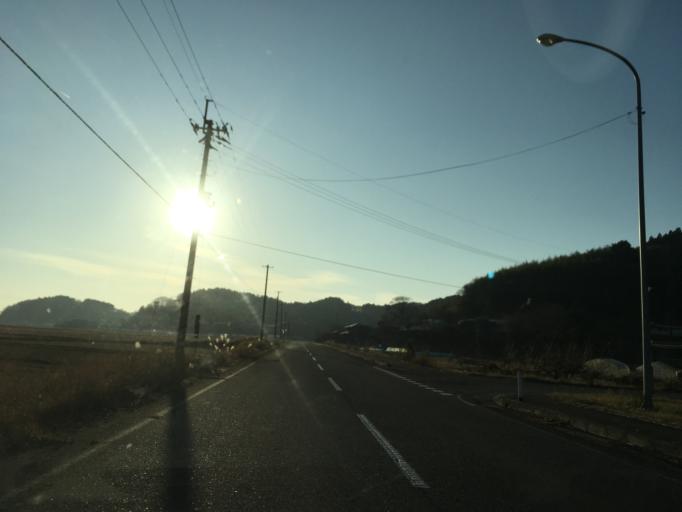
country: JP
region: Iwate
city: Ichinoseki
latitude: 38.7549
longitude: 141.2325
